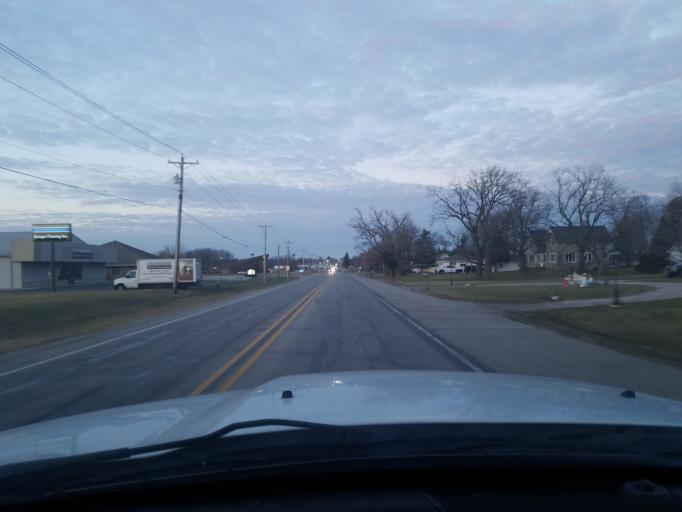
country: US
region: Indiana
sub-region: Wells County
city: Ossian
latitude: 40.8686
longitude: -85.1665
